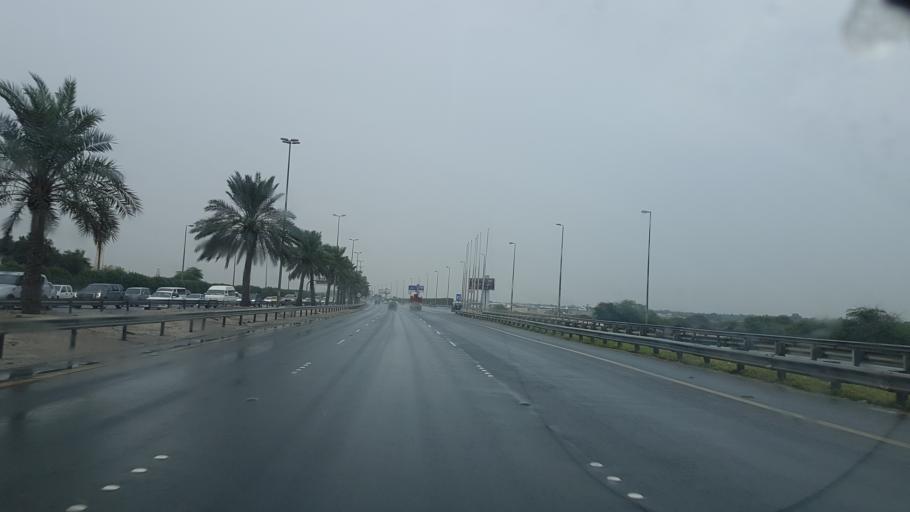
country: BH
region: Northern
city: Madinat `Isa
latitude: 26.1783
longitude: 50.5022
